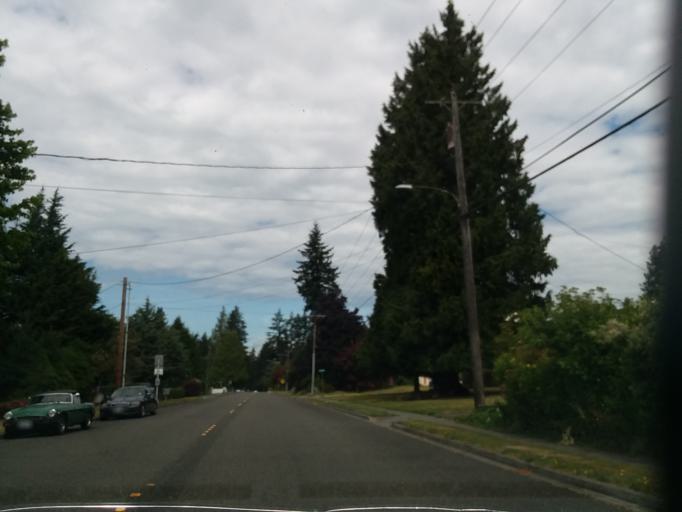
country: US
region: Washington
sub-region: Snohomish County
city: Alderwood Manor
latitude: 47.8308
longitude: -122.2979
